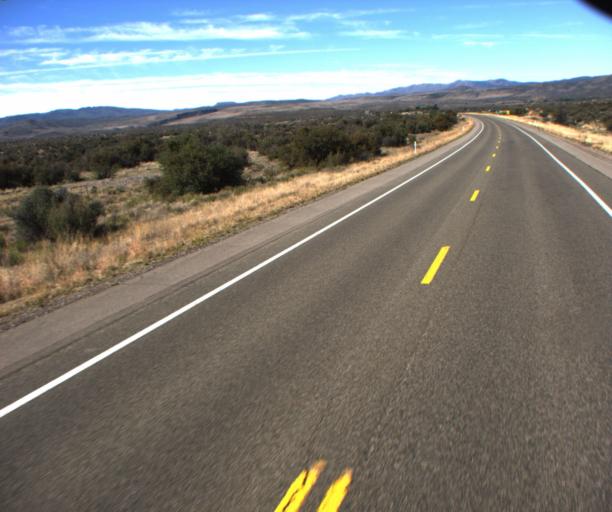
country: US
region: Arizona
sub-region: Yavapai County
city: Prescott
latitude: 34.3828
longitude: -112.6543
